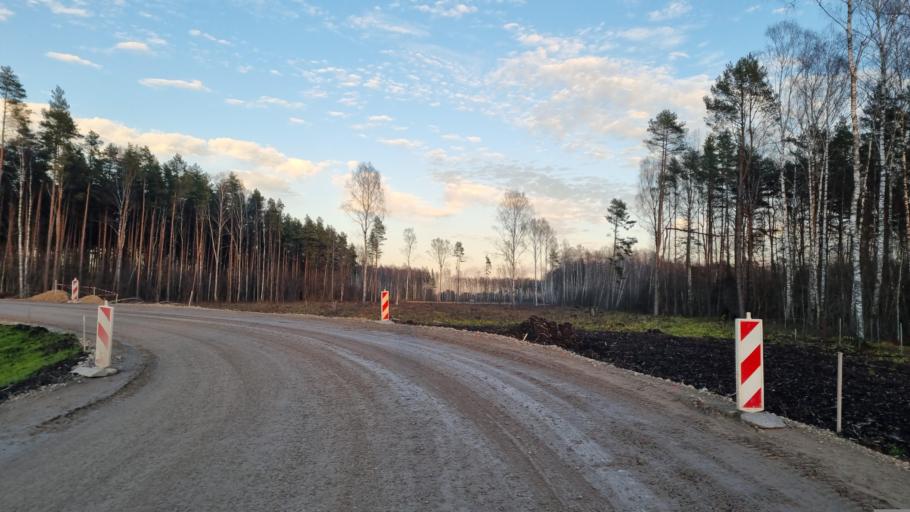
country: LV
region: Kekava
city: Balozi
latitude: 56.8663
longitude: 24.1665
